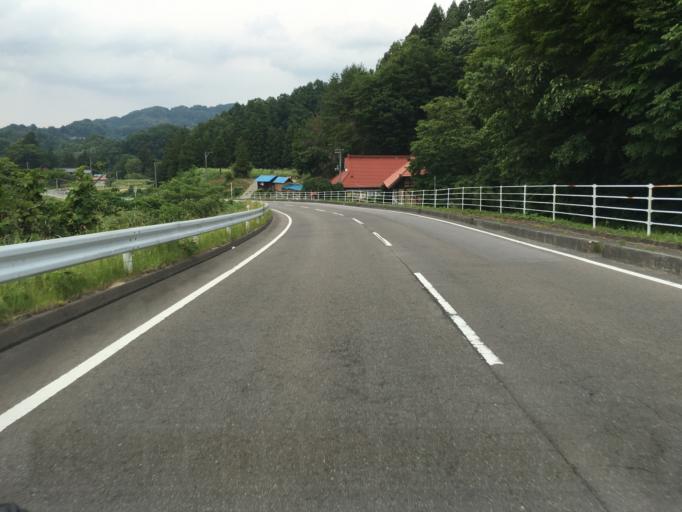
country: JP
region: Fukushima
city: Nihommatsu
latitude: 37.6100
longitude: 140.5596
